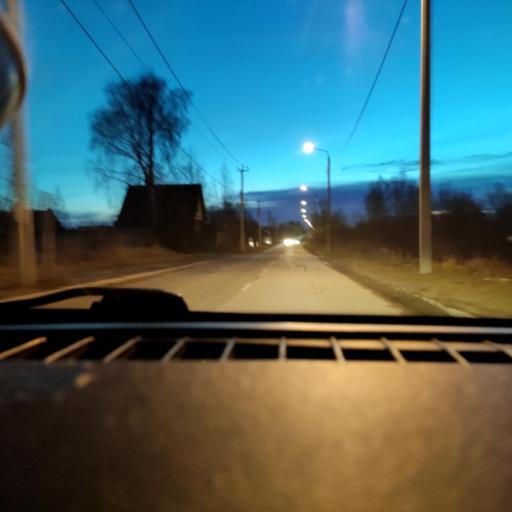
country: RU
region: Perm
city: Perm
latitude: 58.0267
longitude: 56.1848
